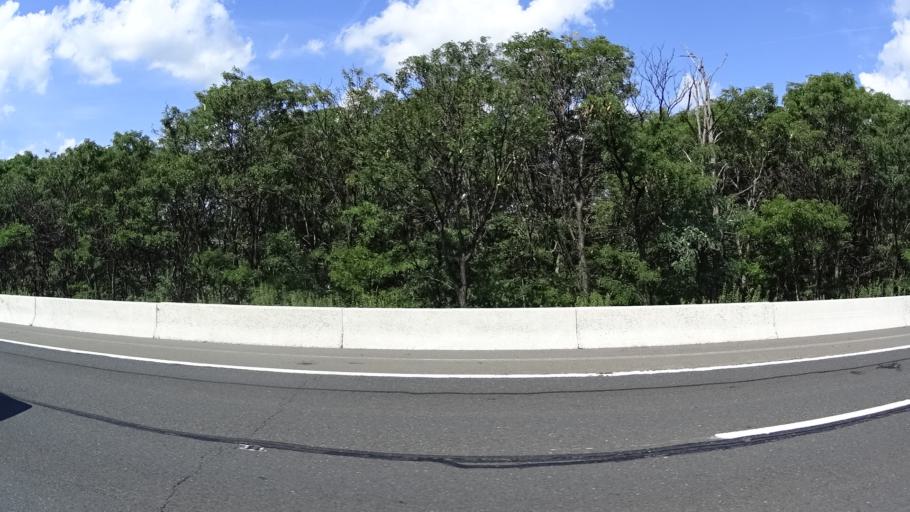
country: US
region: New Jersey
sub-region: Union County
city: Winfield
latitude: 40.6527
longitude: -74.2874
